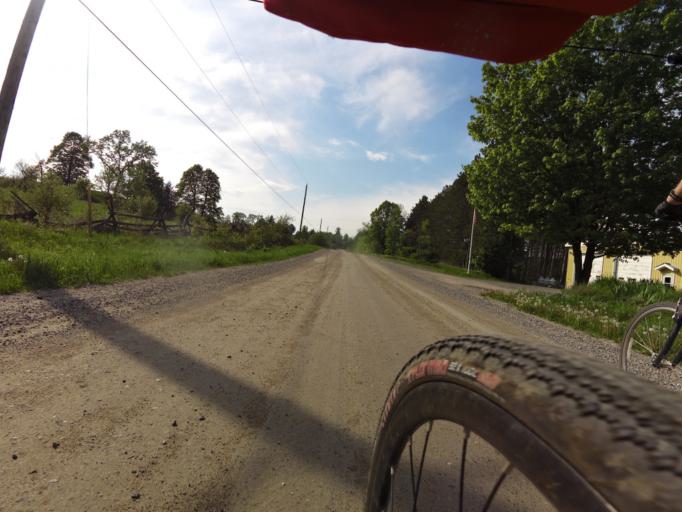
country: CA
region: Ontario
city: Arnprior
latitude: 45.1743
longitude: -76.4703
